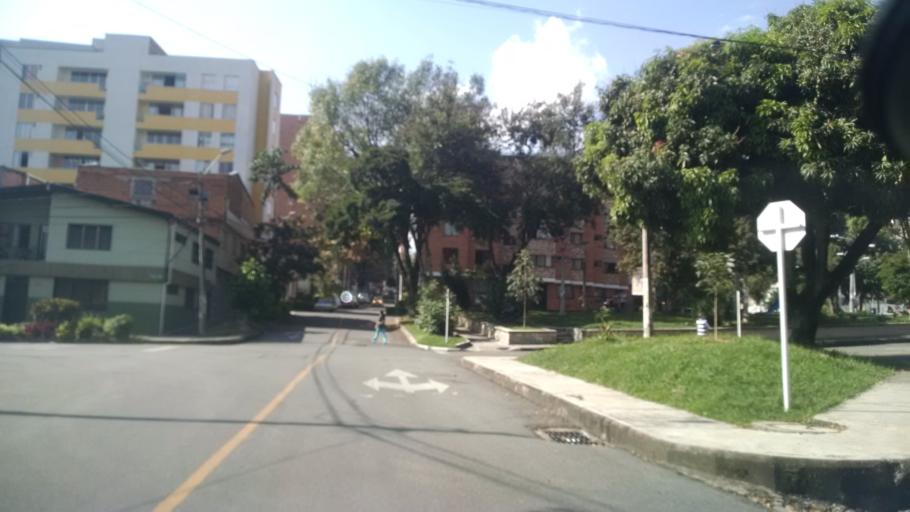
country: CO
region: Antioquia
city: Medellin
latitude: 6.2527
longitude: -75.6054
